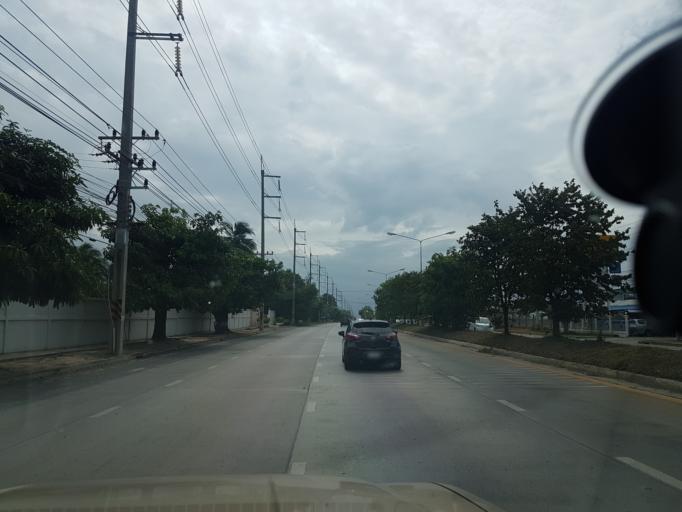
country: TH
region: Sara Buri
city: Phra Phutthabat
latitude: 14.7155
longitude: 100.8174
